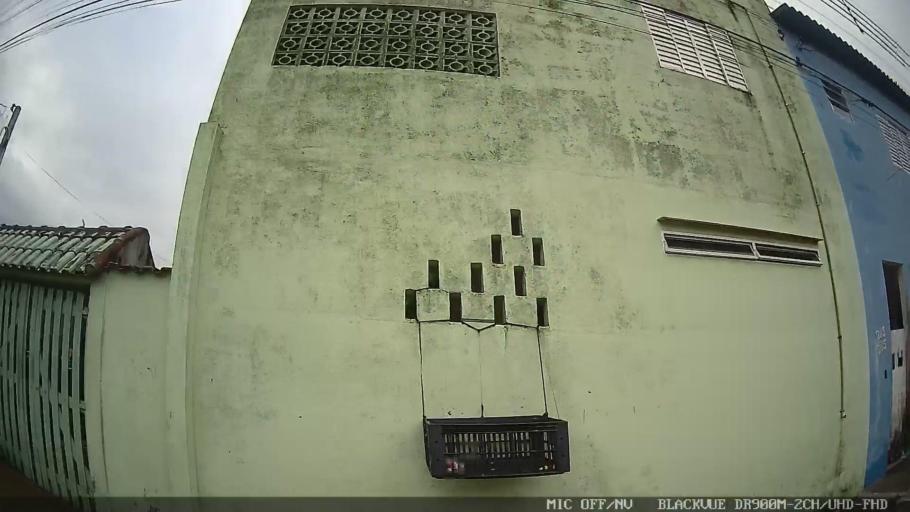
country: BR
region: Sao Paulo
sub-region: Itanhaem
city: Itanhaem
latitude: -24.1772
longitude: -46.8184
